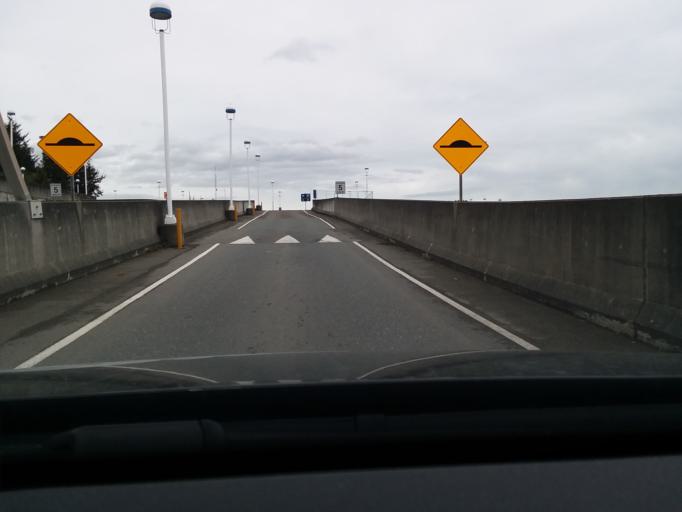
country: CA
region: British Columbia
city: North Saanich
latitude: 48.6872
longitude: -123.4110
